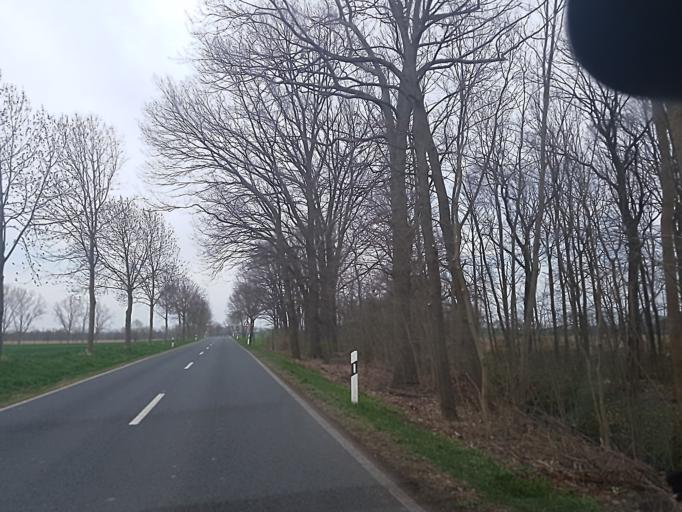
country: DE
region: Saxony
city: Naundorf
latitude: 51.2663
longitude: 13.0827
